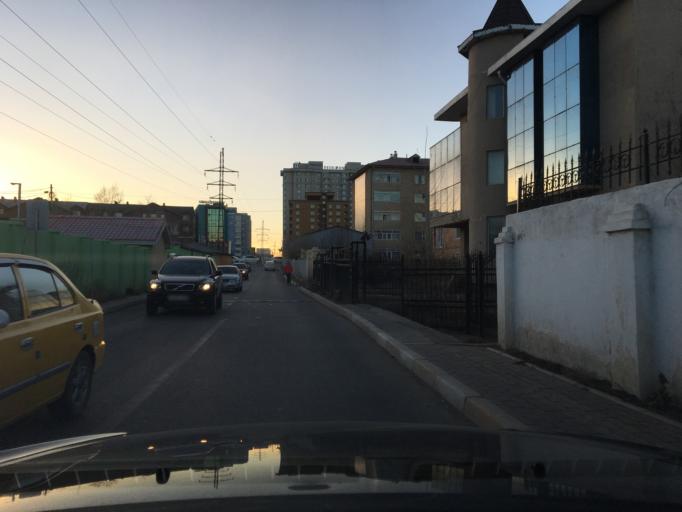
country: MN
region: Ulaanbaatar
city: Ulaanbaatar
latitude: 47.8926
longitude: 106.9108
